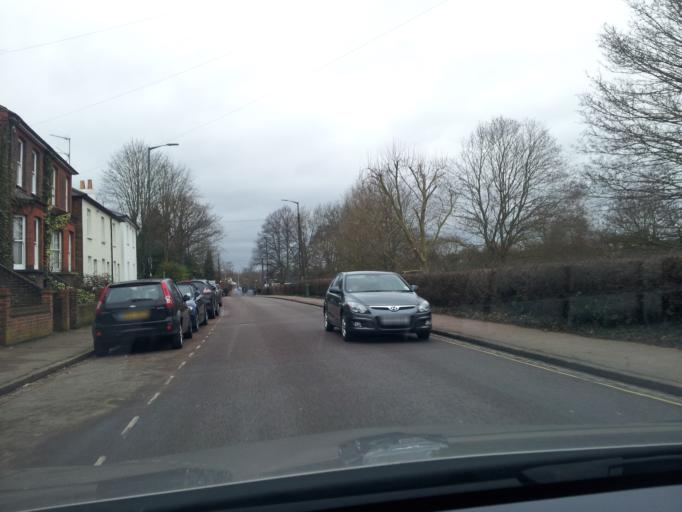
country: GB
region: England
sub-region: Hertfordshire
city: St Albans
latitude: 51.7553
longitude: -0.3461
